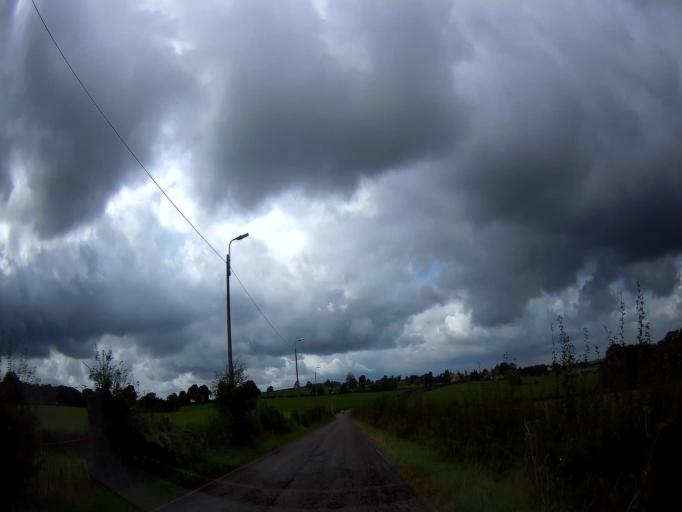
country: BE
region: Wallonia
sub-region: Province de Liege
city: Limbourg
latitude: 50.5963
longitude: 5.9221
